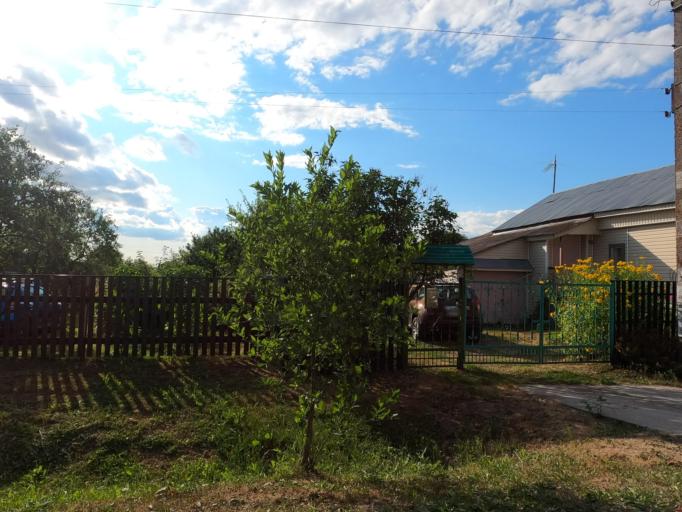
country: RU
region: Moskovskaya
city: Konobeyevo
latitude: 55.4106
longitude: 38.7187
